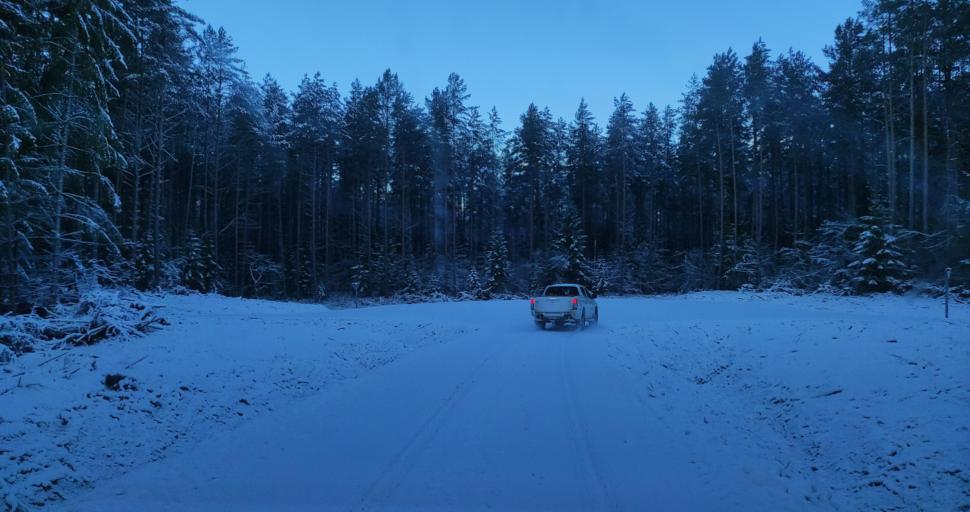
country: LV
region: Skrunda
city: Skrunda
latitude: 56.5935
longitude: 21.9479
